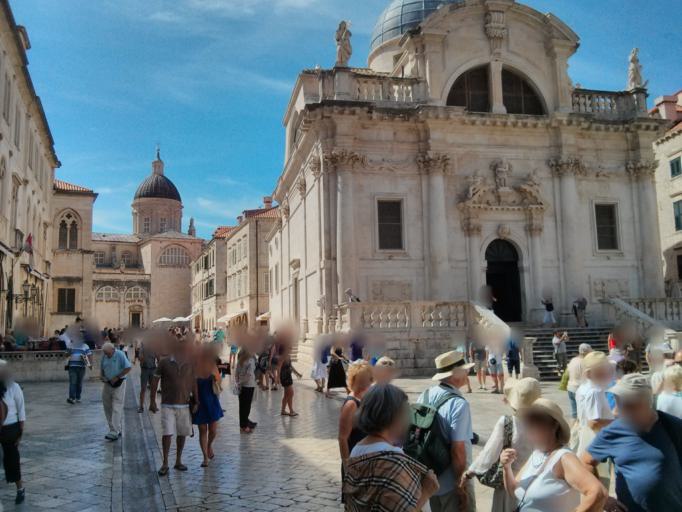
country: HR
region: Dubrovacko-Neretvanska
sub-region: Grad Dubrovnik
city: Dubrovnik
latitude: 42.6410
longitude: 18.1105
